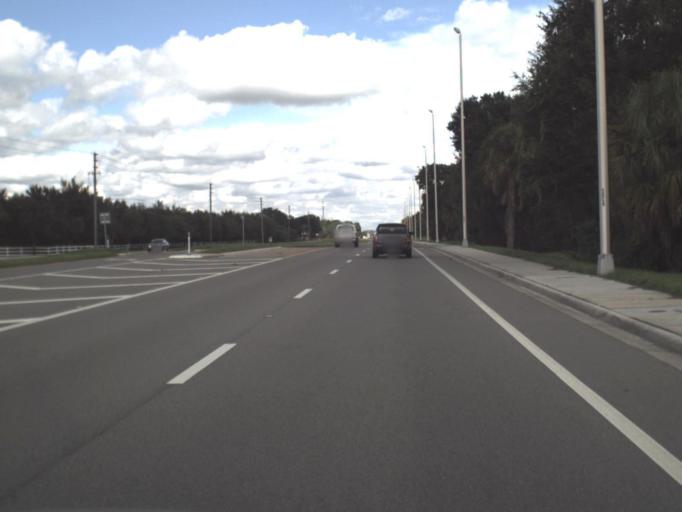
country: US
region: Florida
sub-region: Manatee County
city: Ellenton
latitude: 27.5464
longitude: -82.4700
